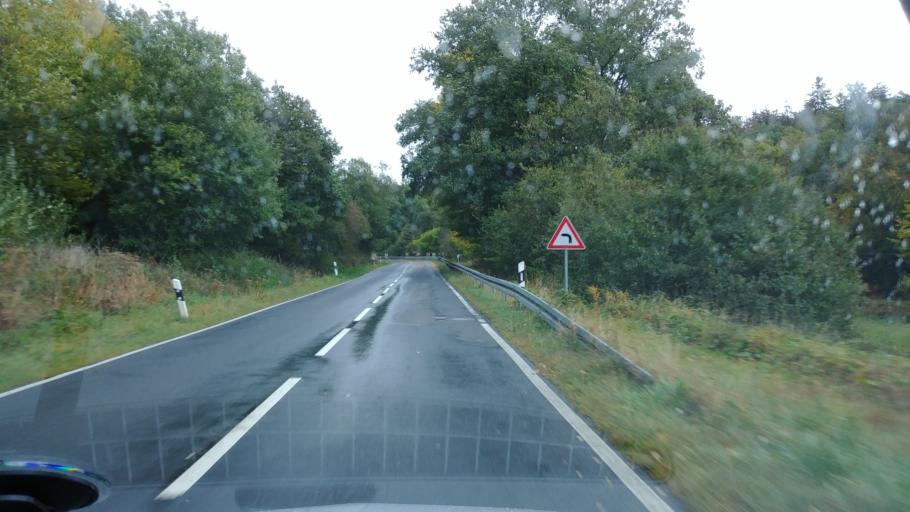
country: DE
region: Hesse
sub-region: Regierungsbezirk Darmstadt
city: Bad Schwalbach
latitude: 50.1507
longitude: 8.1037
